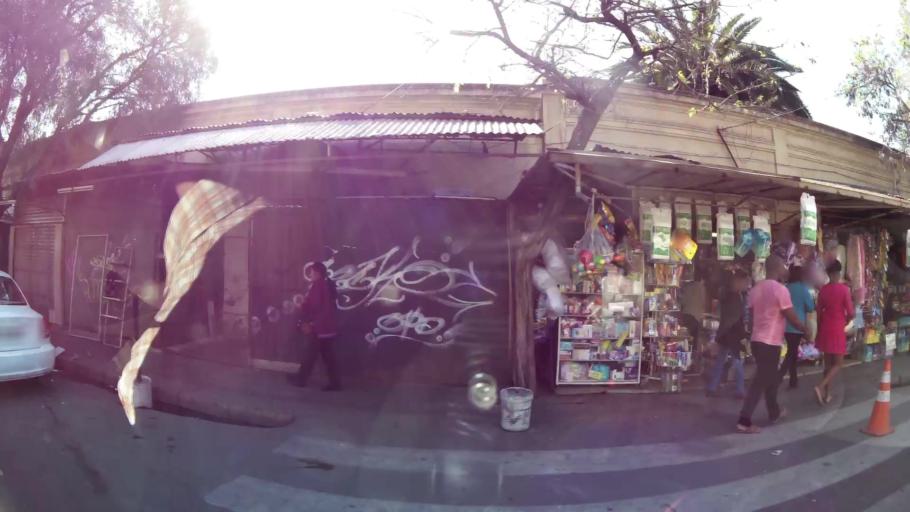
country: CL
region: Santiago Metropolitan
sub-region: Provincia de Santiago
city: Santiago
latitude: -33.4164
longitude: -70.6527
